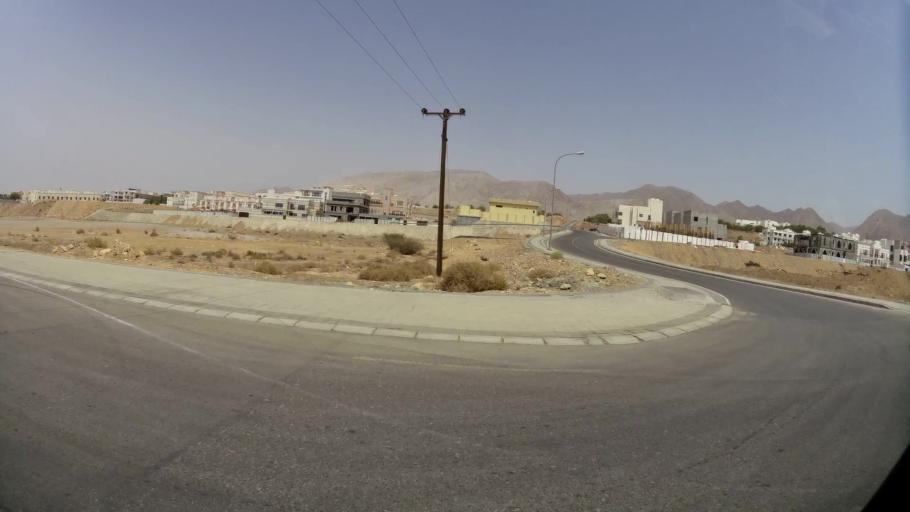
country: OM
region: Muhafazat Masqat
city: Bawshar
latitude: 23.5532
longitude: 58.3925
